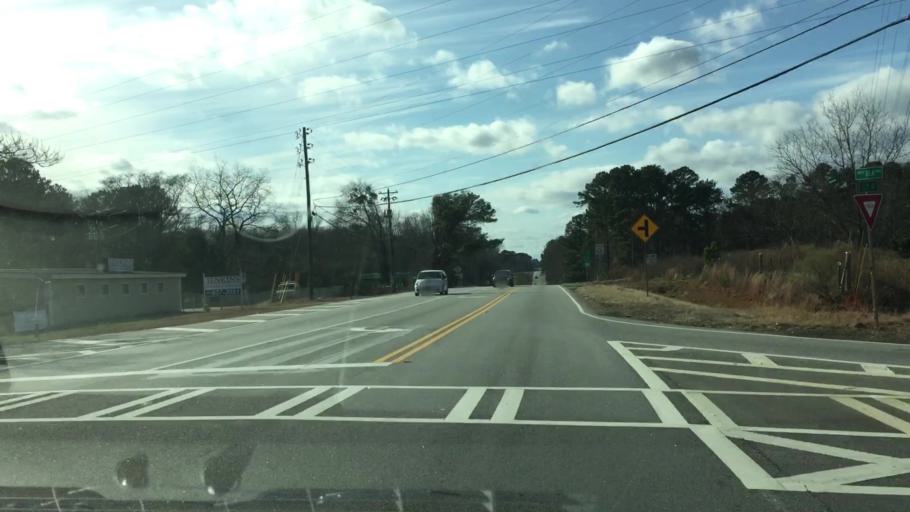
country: US
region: Georgia
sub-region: Henry County
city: McDonough
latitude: 33.4357
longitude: -84.0416
